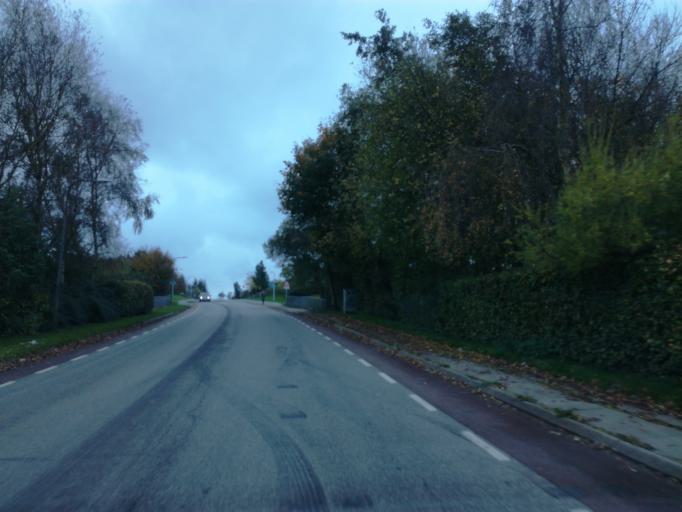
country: DK
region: South Denmark
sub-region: Vejle Kommune
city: Borkop
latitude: 55.6366
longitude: 9.6529
